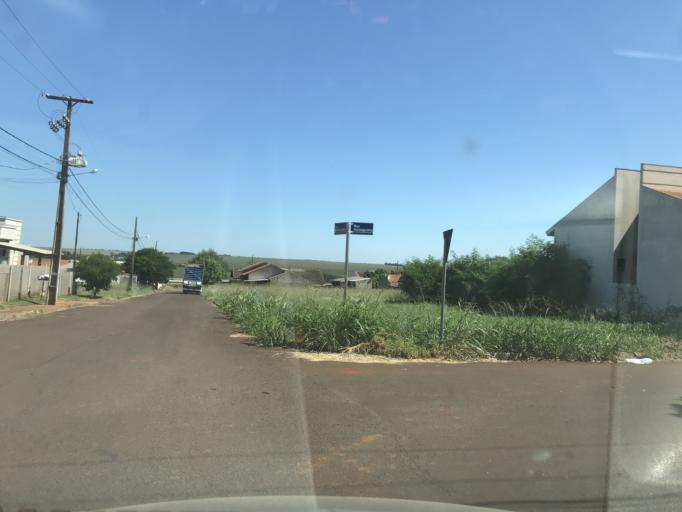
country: BR
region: Parana
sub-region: Palotina
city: Palotina
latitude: -24.3020
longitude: -53.8388
